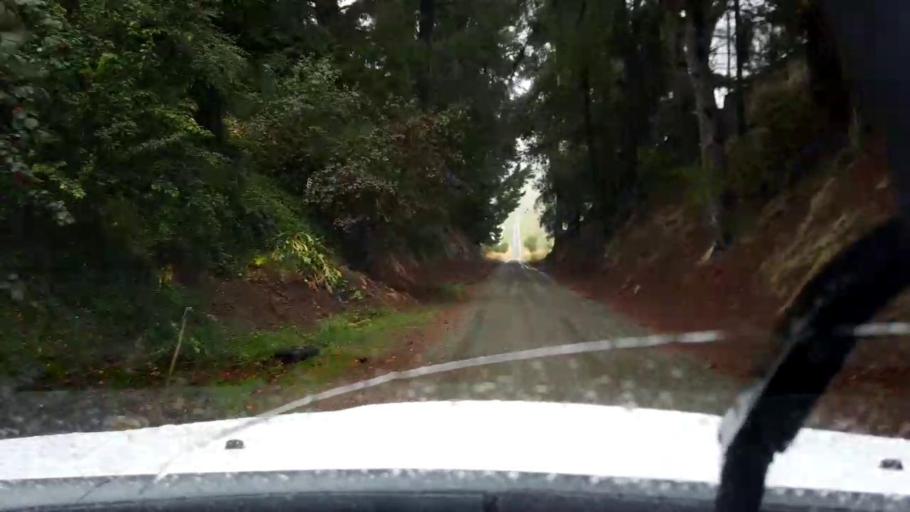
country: NZ
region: Canterbury
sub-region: Timaru District
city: Pleasant Point
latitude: -44.1957
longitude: 171.0914
